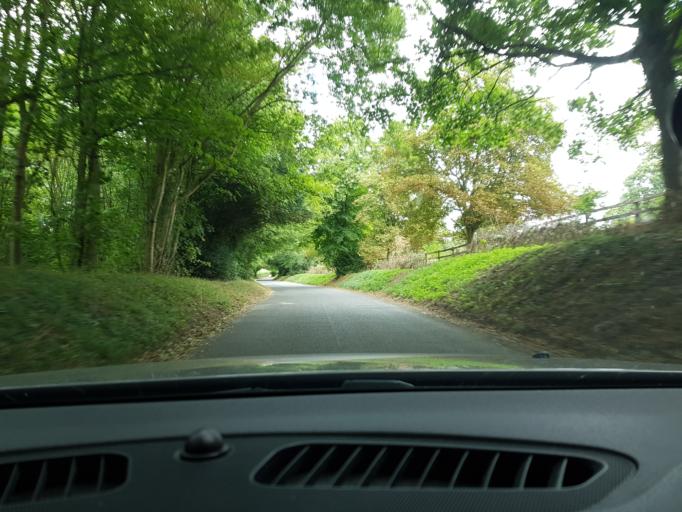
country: GB
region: England
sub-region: West Berkshire
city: Farnborough
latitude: 51.5122
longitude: -1.4068
